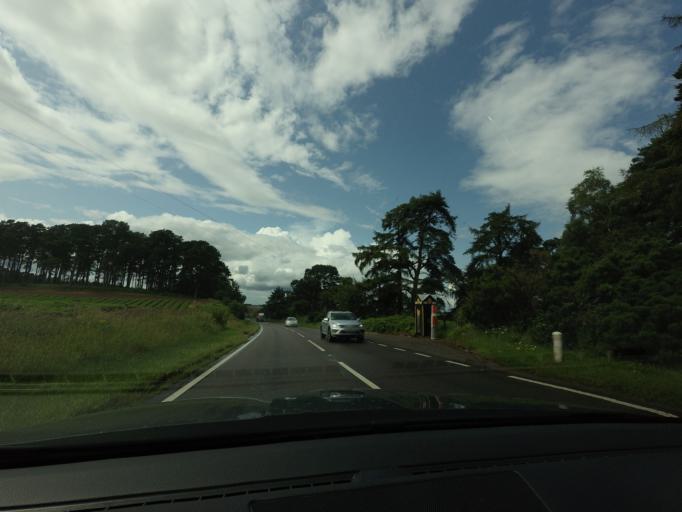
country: GB
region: Scotland
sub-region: Moray
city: Lhanbryd
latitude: 57.6341
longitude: -3.1901
